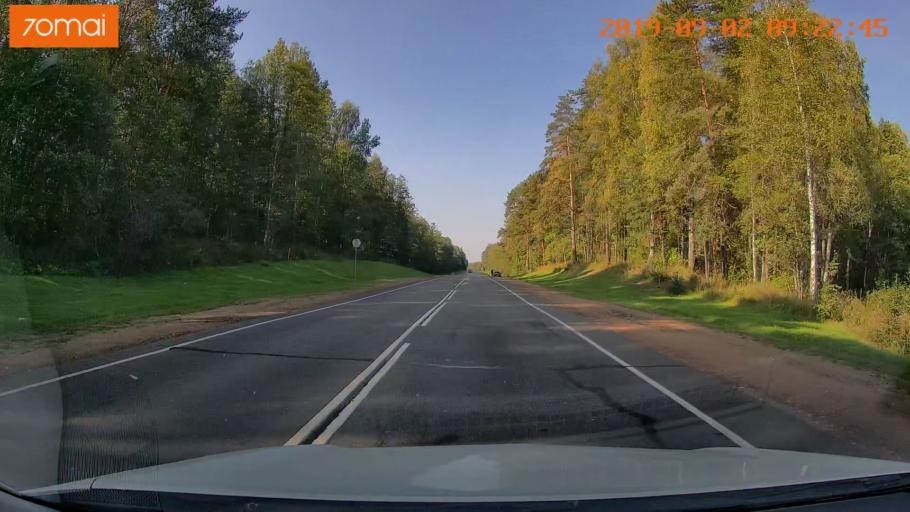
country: RU
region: Kaluga
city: Yukhnov
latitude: 54.7820
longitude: 35.3312
